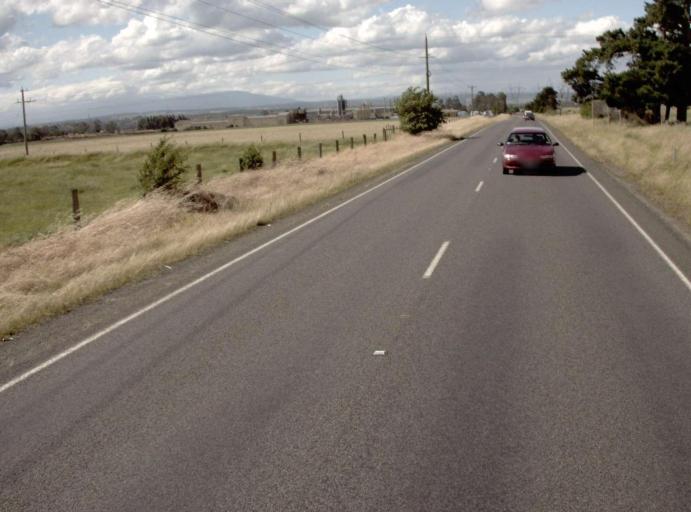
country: AU
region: Victoria
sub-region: Latrobe
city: Morwell
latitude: -38.2719
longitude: 146.4333
